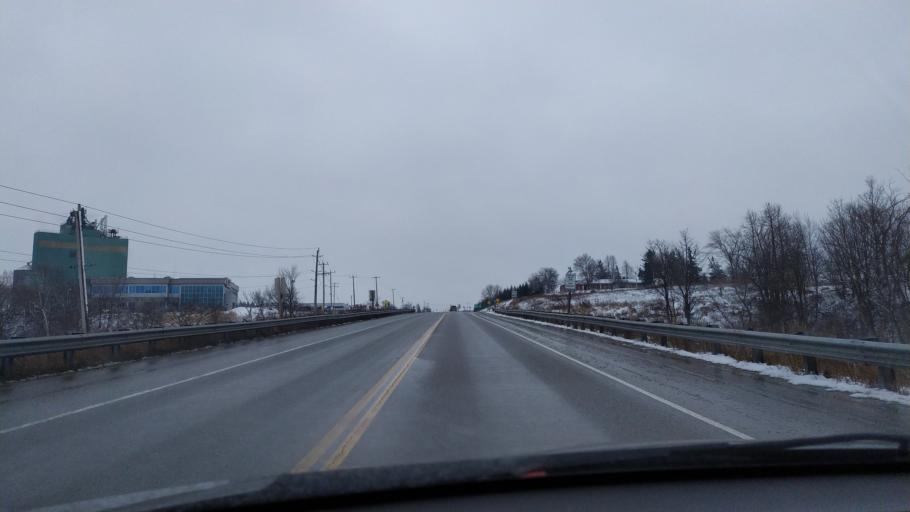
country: CA
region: Ontario
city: Waterloo
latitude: 43.6023
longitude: -80.6410
